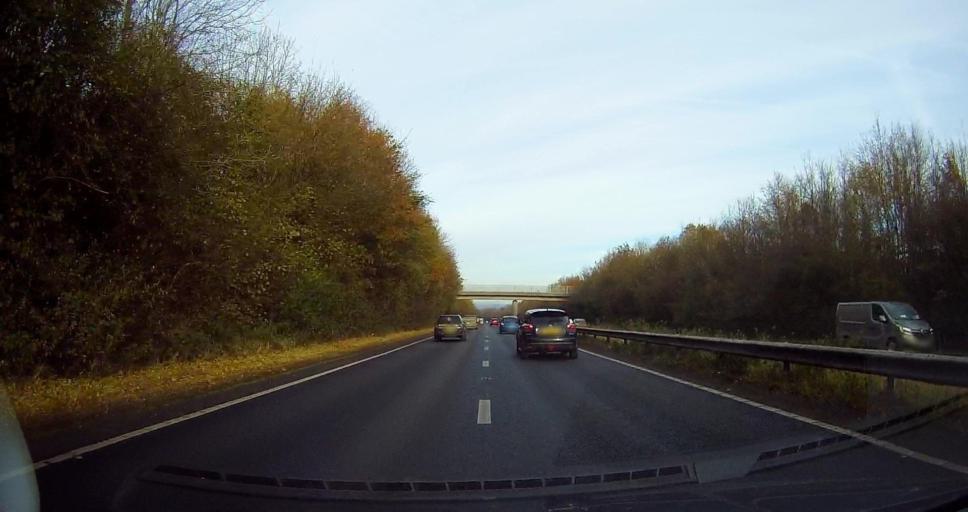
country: GB
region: England
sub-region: West Sussex
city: Hurstpierpoint
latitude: 50.9447
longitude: -0.1940
